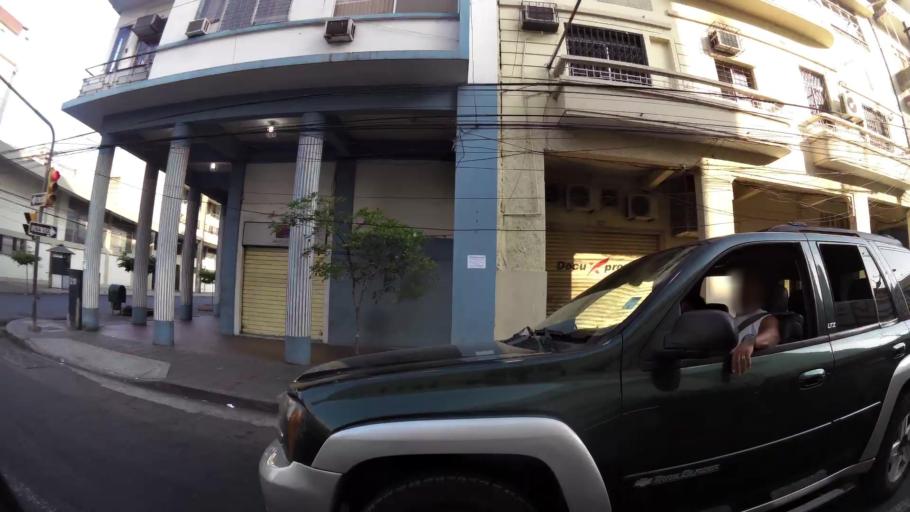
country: EC
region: Guayas
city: Eloy Alfaro
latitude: -2.1887
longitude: -79.8807
